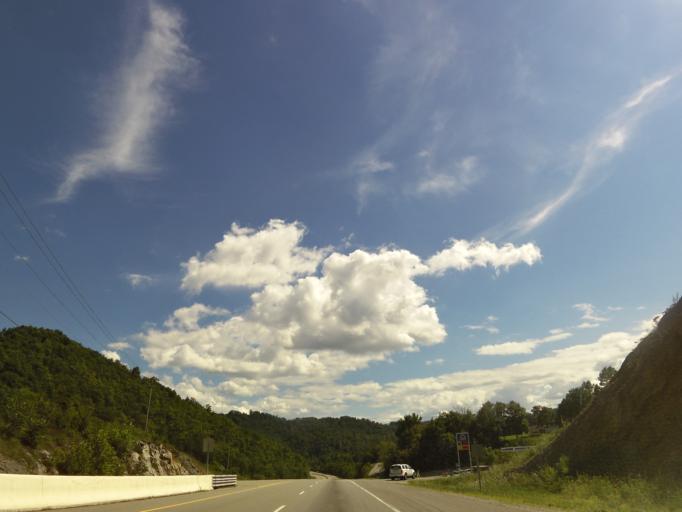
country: US
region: Tennessee
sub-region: Grainger County
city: Rutledge
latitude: 36.3875
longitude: -83.4474
